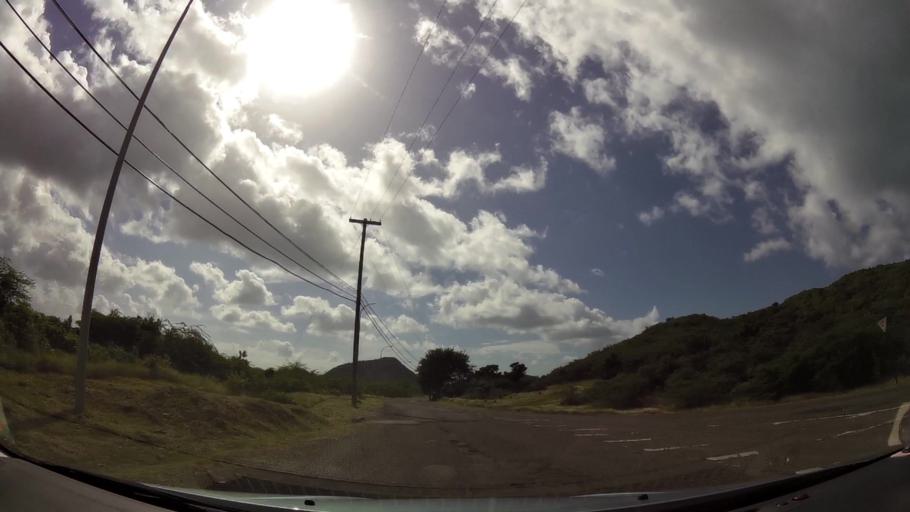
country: AG
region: Saint John
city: Saint John's
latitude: 17.1177
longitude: -61.8690
